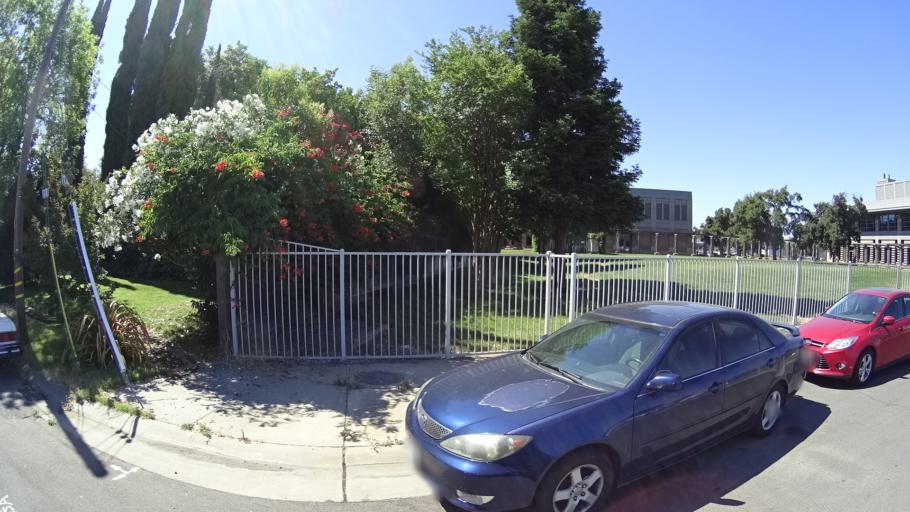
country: US
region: California
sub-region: Sacramento County
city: Parkway
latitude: 38.5507
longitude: -121.4464
